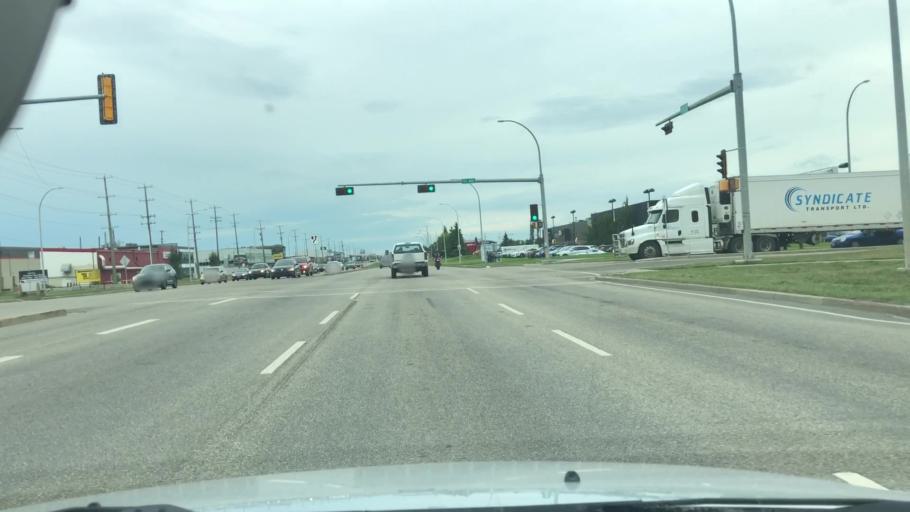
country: CA
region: Alberta
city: St. Albert
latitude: 53.5599
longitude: -113.6154
